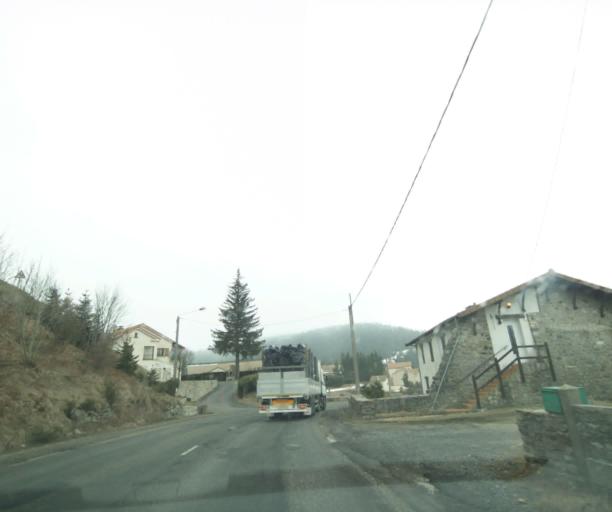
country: FR
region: Languedoc-Roussillon
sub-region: Departement de la Lozere
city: Langogne
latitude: 44.7276
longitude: 4.0076
